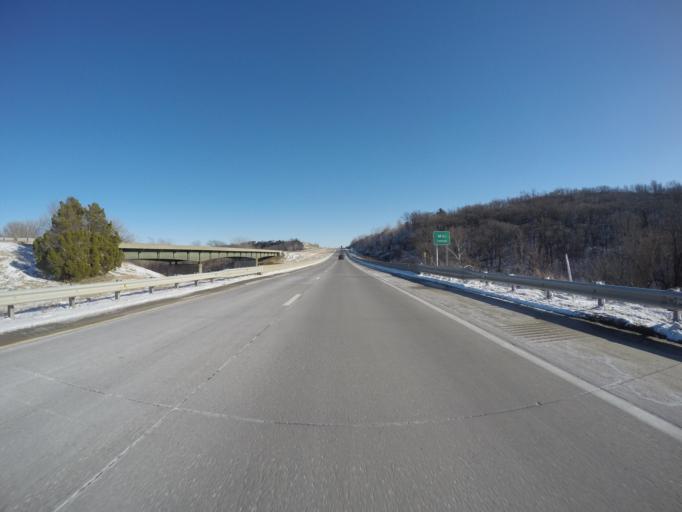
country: US
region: Kansas
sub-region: Wabaunsee County
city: Alma
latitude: 39.0627
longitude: -96.1827
